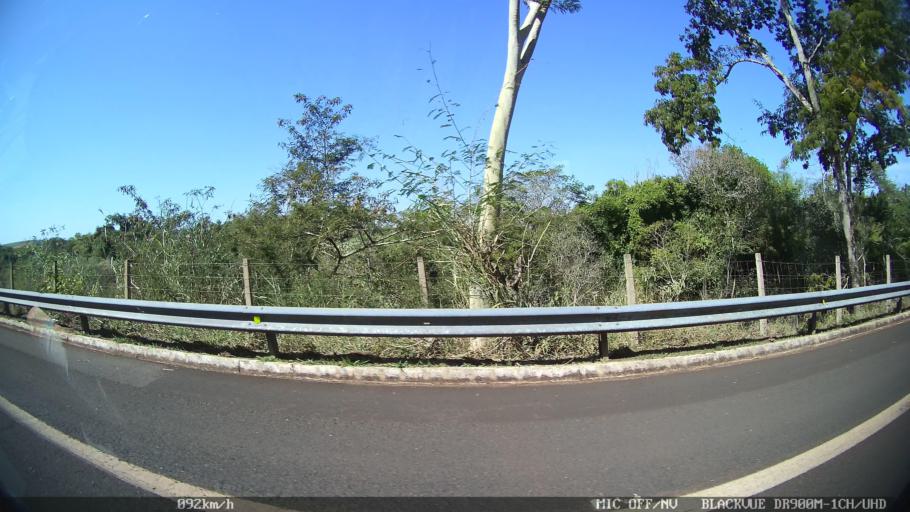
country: BR
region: Sao Paulo
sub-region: Batatais
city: Batatais
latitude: -20.7282
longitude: -47.5198
